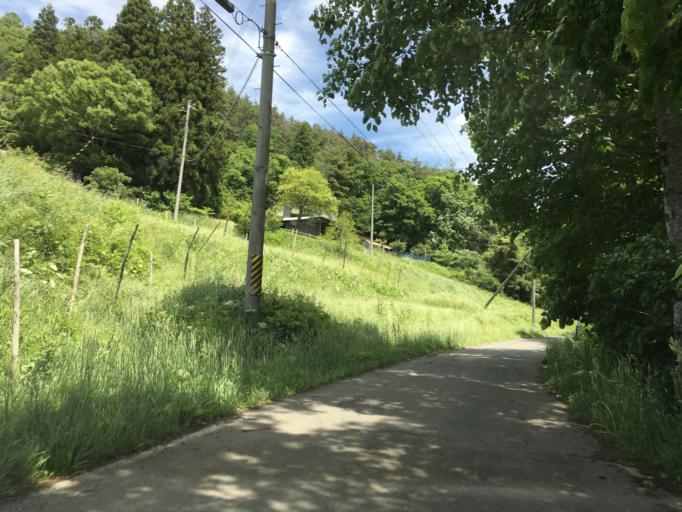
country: JP
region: Iwate
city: Mizusawa
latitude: 39.1278
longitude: 141.2725
